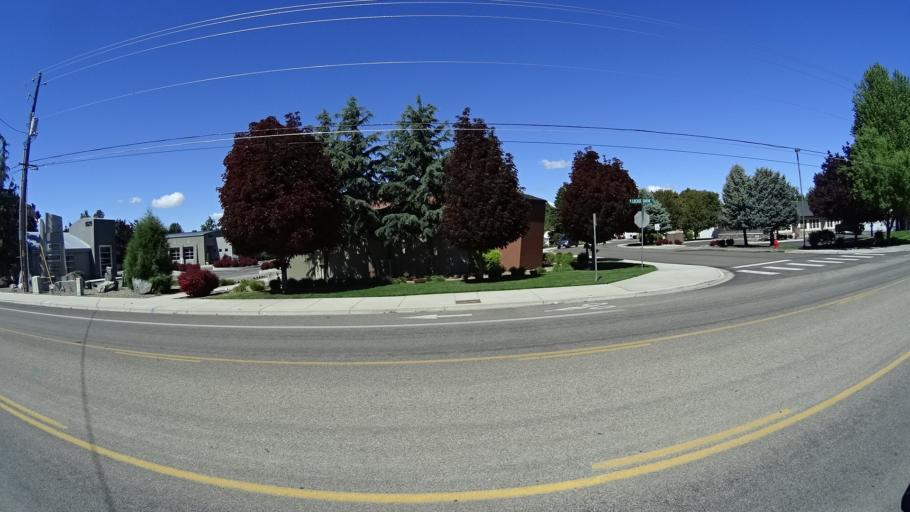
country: US
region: Idaho
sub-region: Ada County
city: Meridian
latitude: 43.6228
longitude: -116.3745
